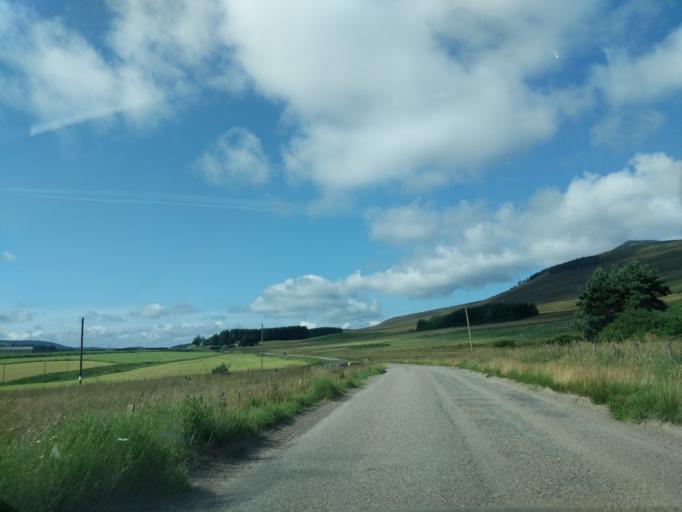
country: GB
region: Scotland
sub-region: Moray
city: Dufftown
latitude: 57.4047
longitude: -3.1841
